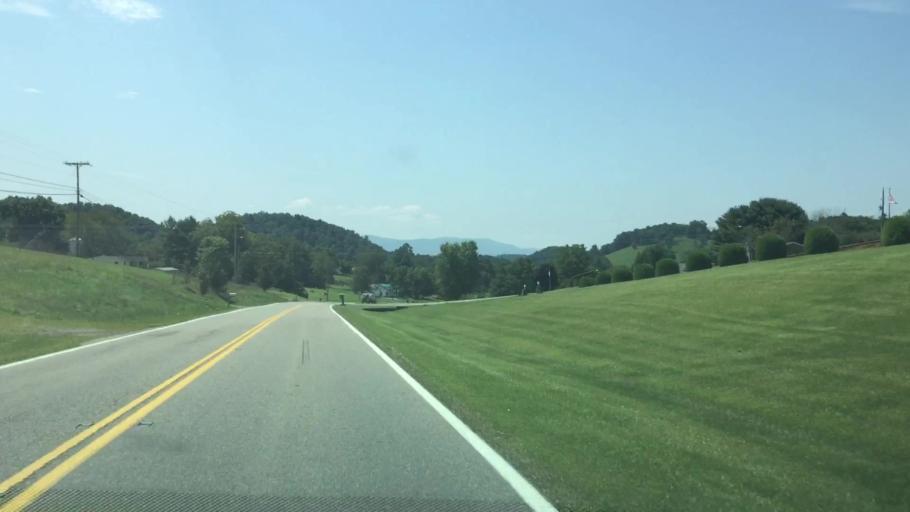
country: US
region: Virginia
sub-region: Washington County
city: Abingdon
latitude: 36.6626
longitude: -81.9665
